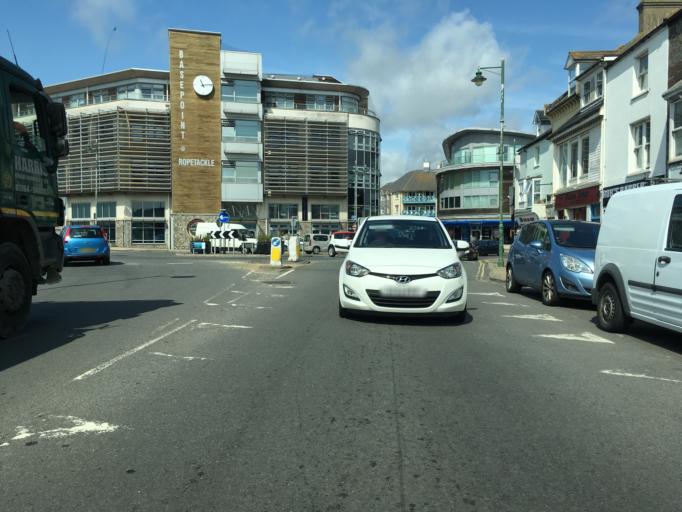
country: GB
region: England
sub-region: West Sussex
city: Shoreham-by-Sea
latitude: 50.8325
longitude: -0.2782
